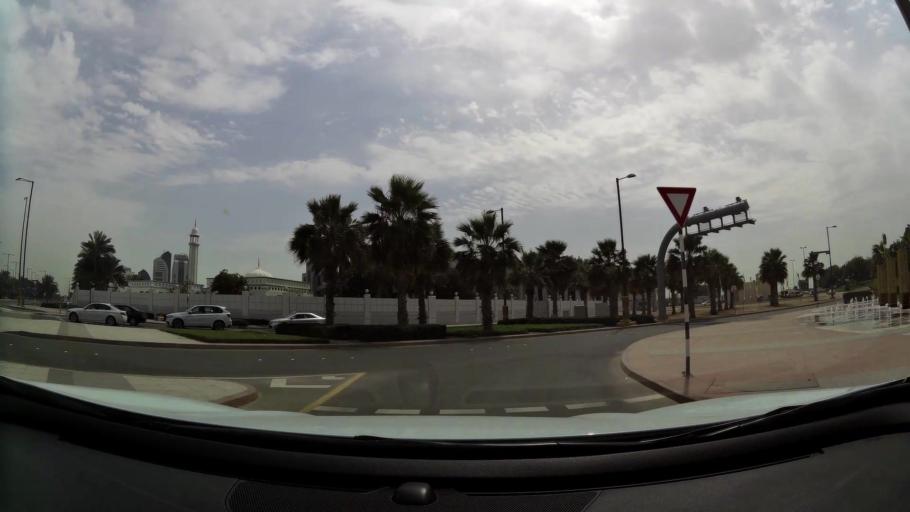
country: AE
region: Abu Dhabi
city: Abu Dhabi
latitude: 24.4584
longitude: 54.3307
